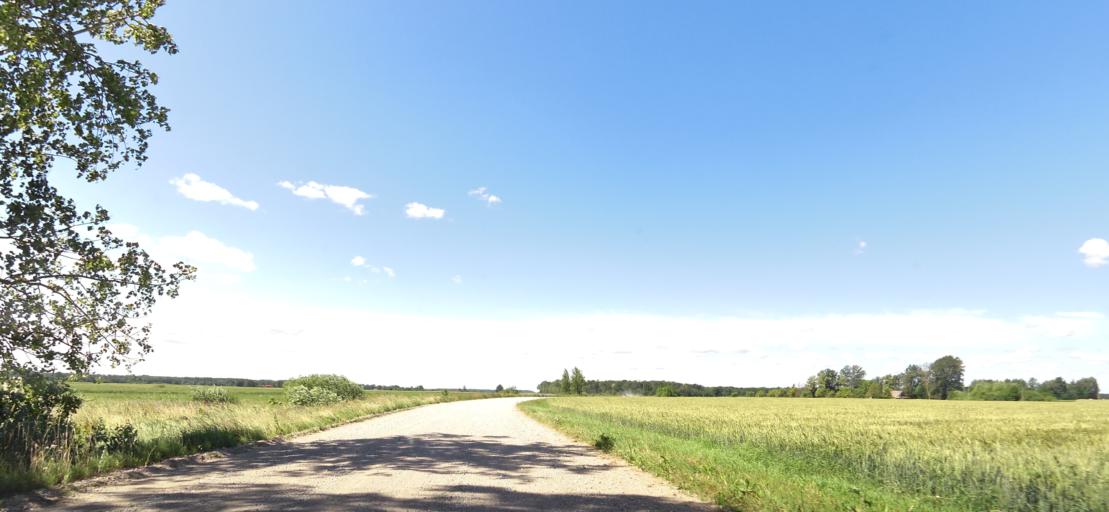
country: LT
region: Panevezys
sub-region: Birzai
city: Birzai
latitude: 56.2745
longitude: 24.5963
